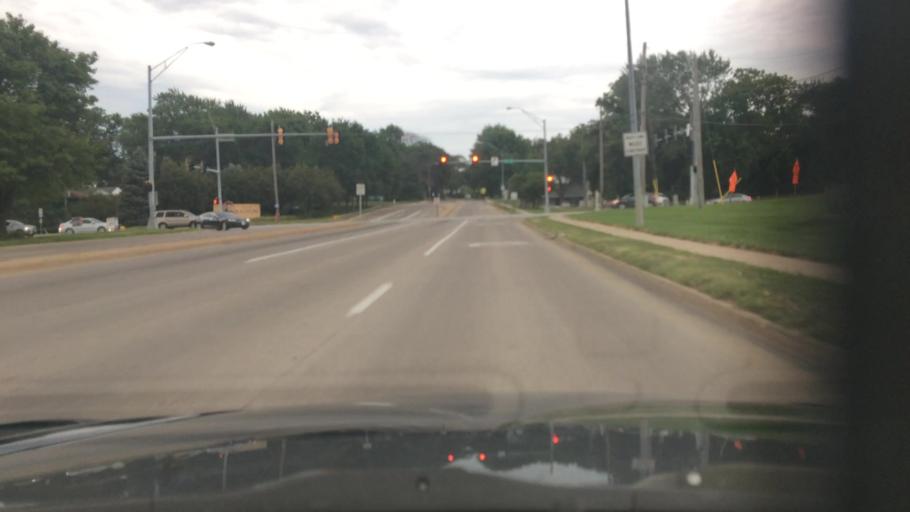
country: US
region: Nebraska
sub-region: Douglas County
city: Ralston
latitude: 41.2052
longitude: -96.0439
